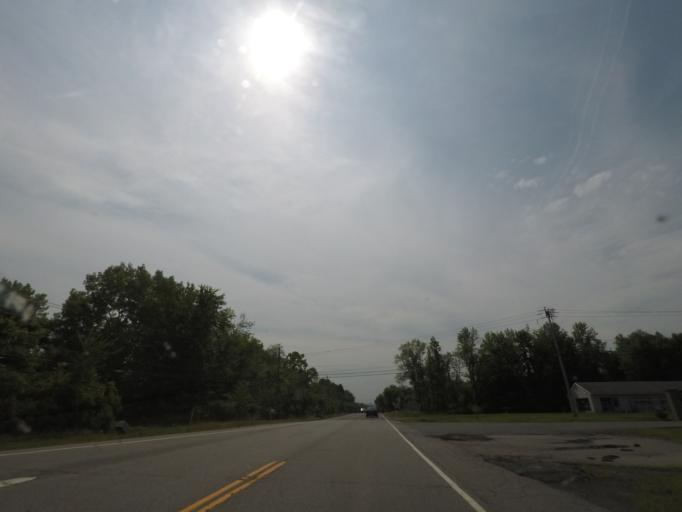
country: US
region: New York
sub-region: Saratoga County
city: Mechanicville
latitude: 42.8821
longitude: -73.6851
